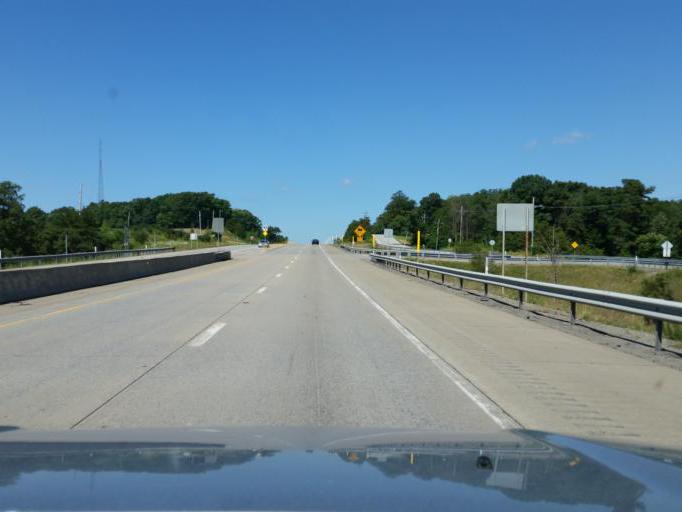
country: US
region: Pennsylvania
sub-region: Cambria County
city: Vinco
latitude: 40.4423
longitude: -78.9559
